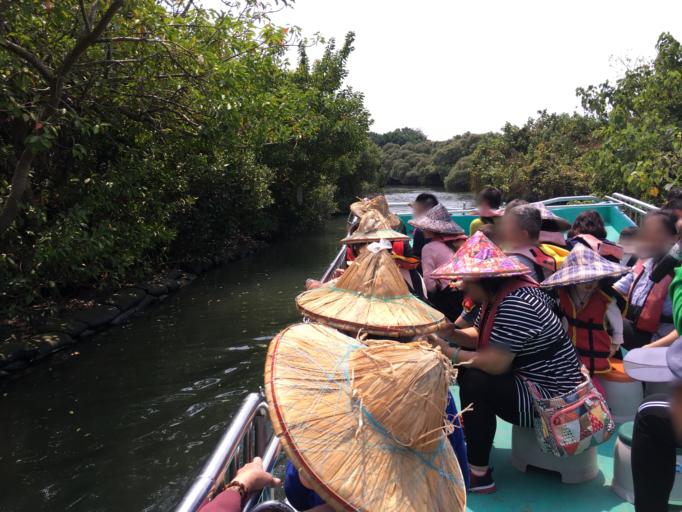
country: TW
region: Taiwan
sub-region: Tainan
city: Tainan
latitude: 23.0221
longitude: 120.1344
